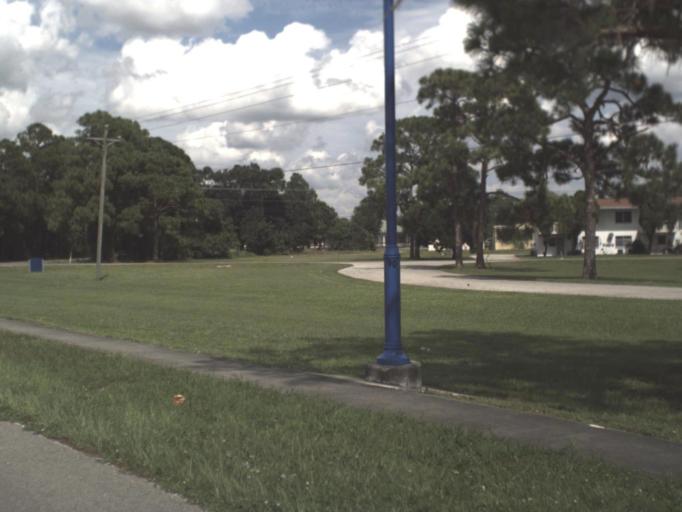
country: US
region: Florida
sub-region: Collier County
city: Immokalee
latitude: 26.4393
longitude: -81.4339
